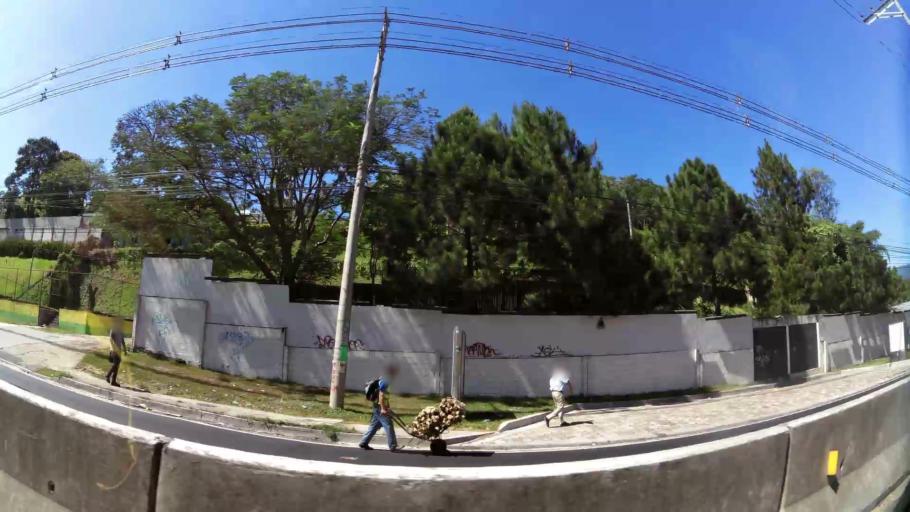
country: SV
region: La Libertad
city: Santa Tecla
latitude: 13.6604
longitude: -89.2790
